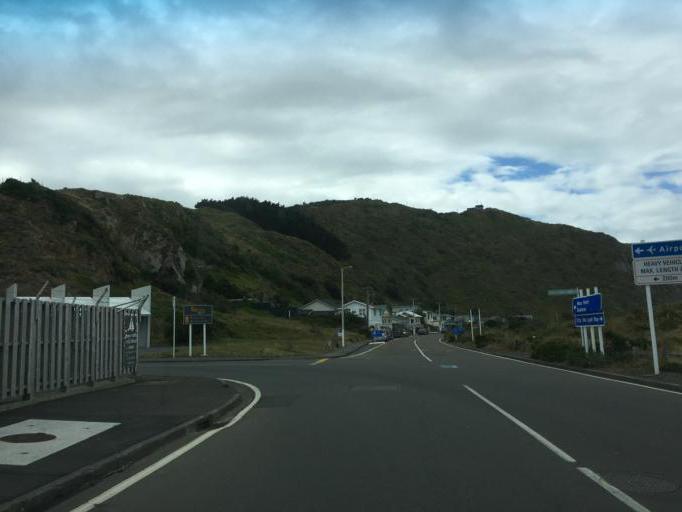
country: NZ
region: Wellington
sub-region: Wellington City
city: Wellington
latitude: -41.3360
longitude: 174.8090
